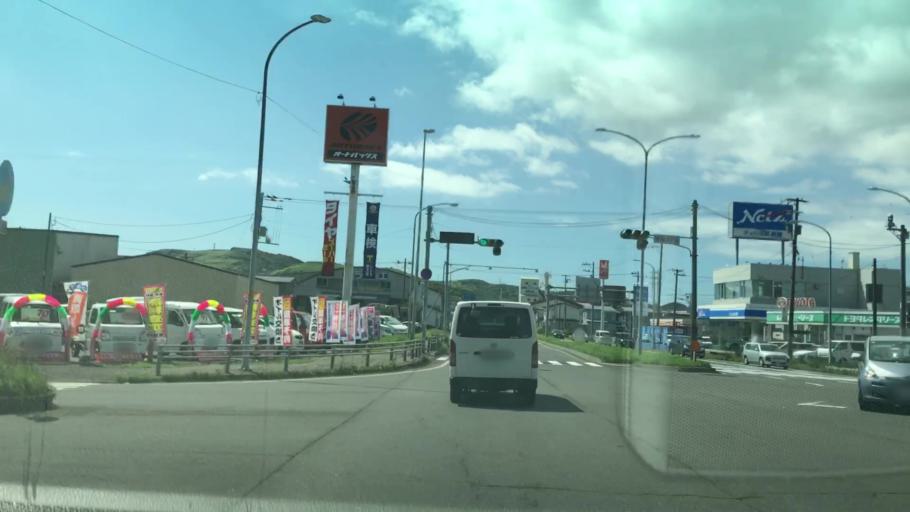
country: JP
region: Hokkaido
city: Muroran
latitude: 42.3405
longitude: 141.0293
